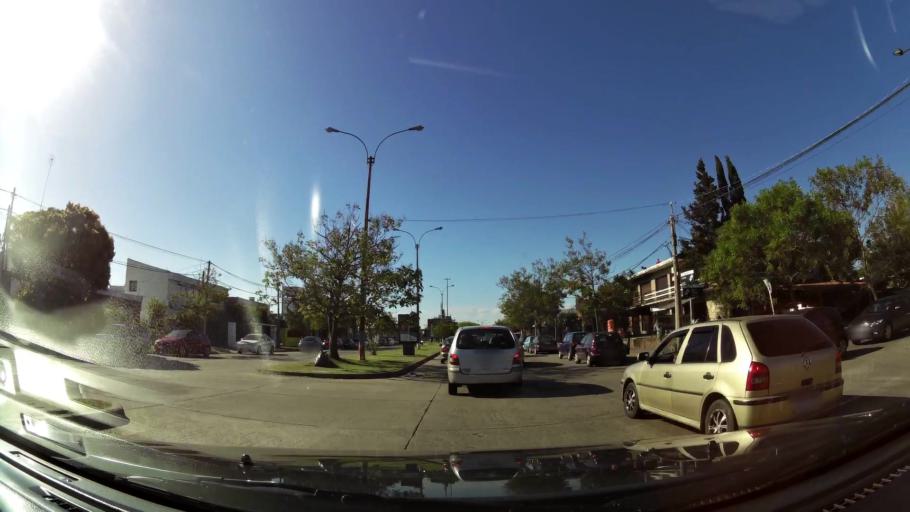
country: UY
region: Canelones
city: Paso de Carrasco
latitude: -34.8845
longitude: -56.0828
